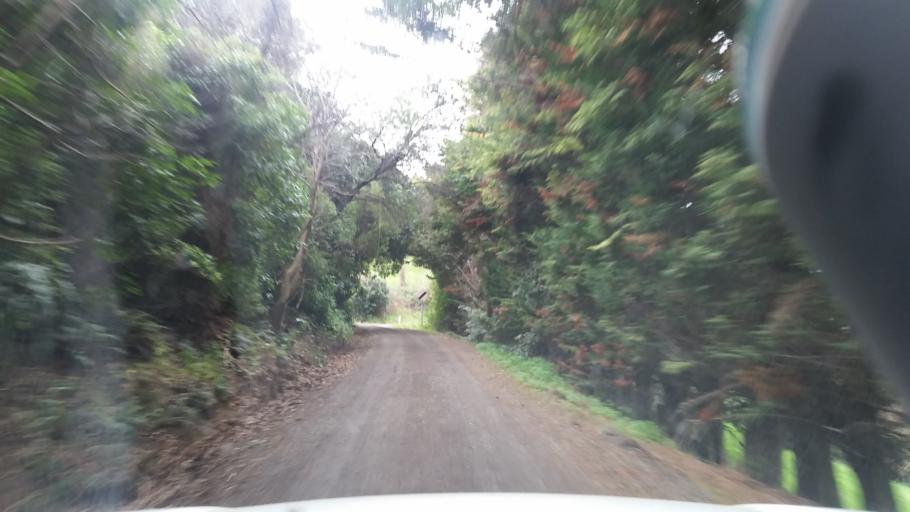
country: NZ
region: Canterbury
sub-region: Christchurch City
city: Christchurch
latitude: -43.7965
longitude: 172.9722
